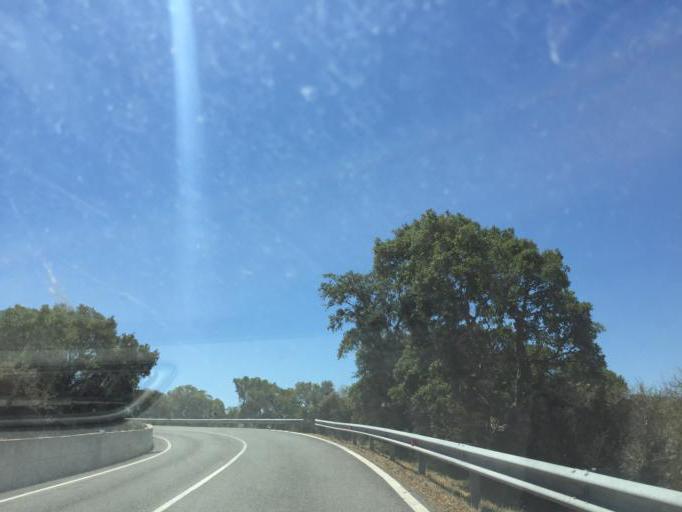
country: IT
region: Sardinia
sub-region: Provincia di Olbia-Tempio
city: Telti
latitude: 40.8922
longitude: 9.3040
